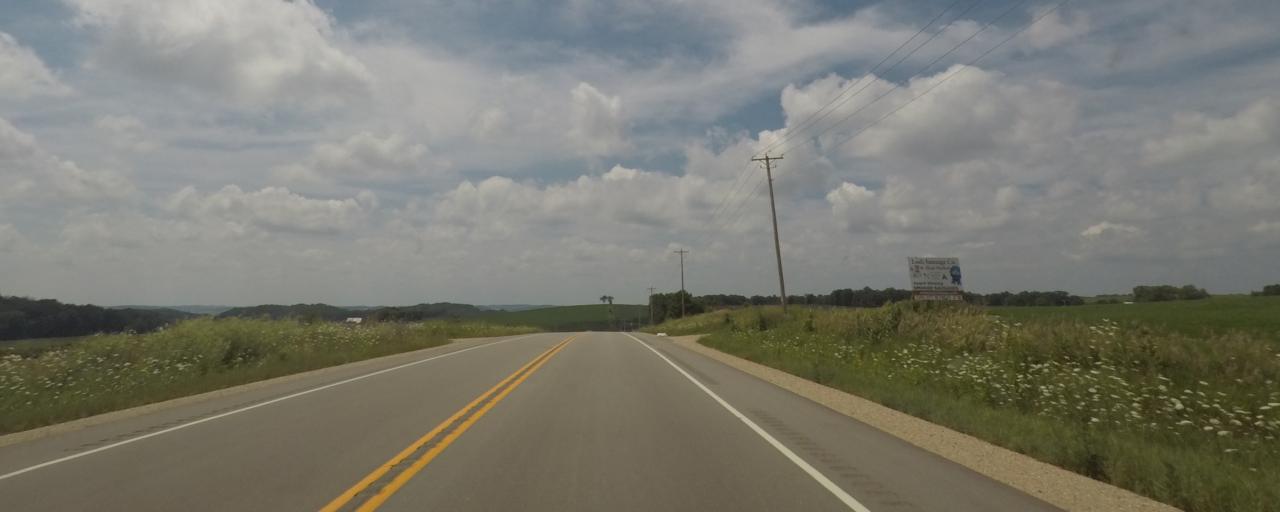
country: US
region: Wisconsin
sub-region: Columbia County
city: Lodi
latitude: 43.3303
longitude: -89.4769
